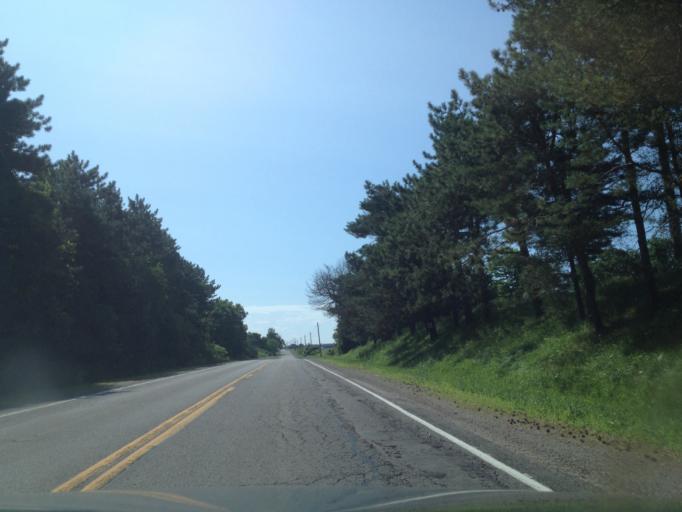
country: CA
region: Ontario
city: Norfolk County
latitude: 42.7546
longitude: -80.3808
